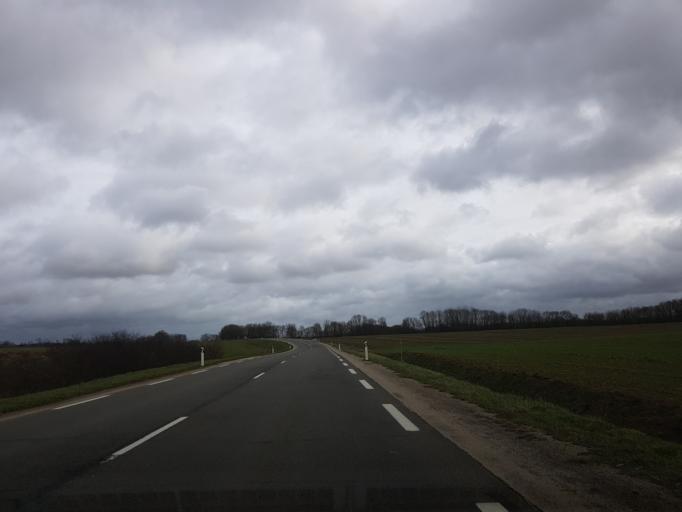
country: FR
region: Champagne-Ardenne
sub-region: Departement de la Haute-Marne
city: Chalindrey
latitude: 47.8443
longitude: 5.4520
